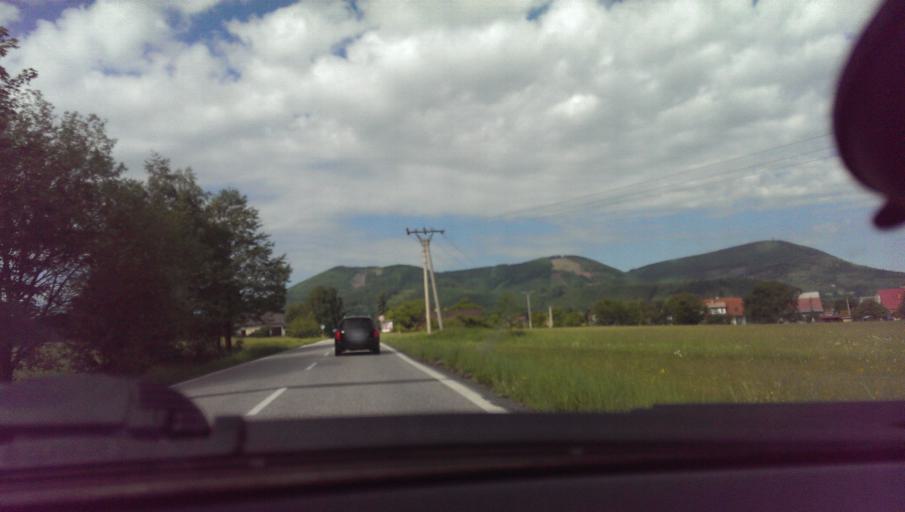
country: CZ
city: Trojanovice
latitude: 49.5201
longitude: 18.2207
